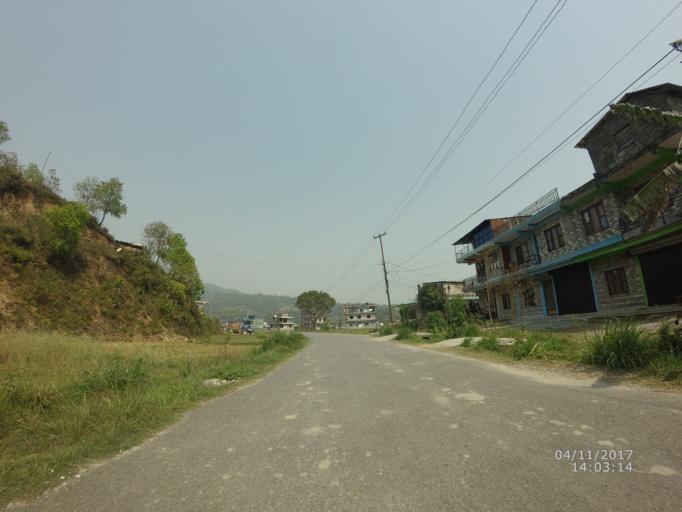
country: NP
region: Western Region
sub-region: Gandaki Zone
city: Pokhara
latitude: 28.1857
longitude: 84.0478
